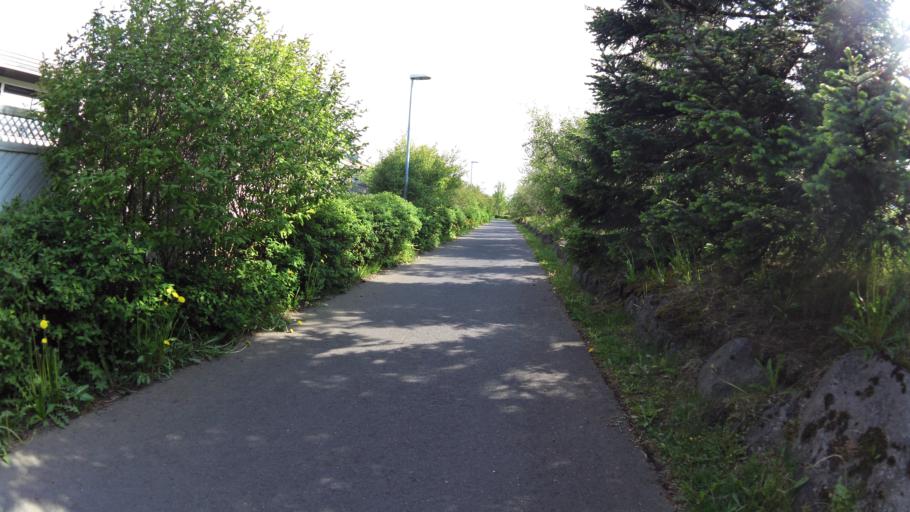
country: IS
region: Capital Region
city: Reykjavik
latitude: 64.1089
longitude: -21.8404
